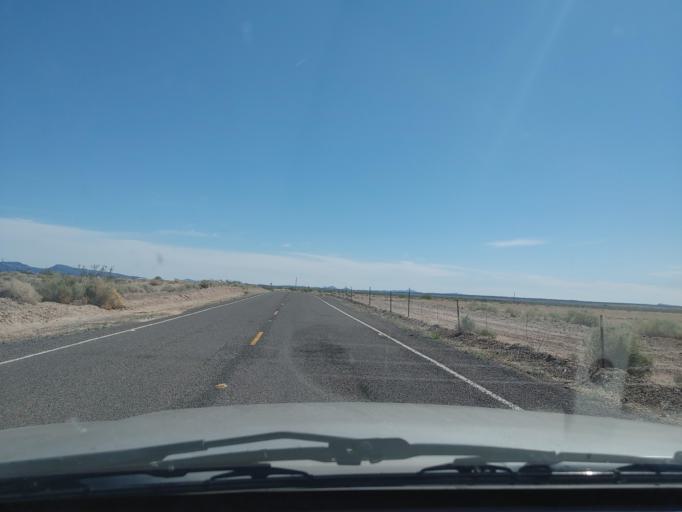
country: US
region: Arizona
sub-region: Maricopa County
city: Gila Bend
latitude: 32.9864
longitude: -113.3098
